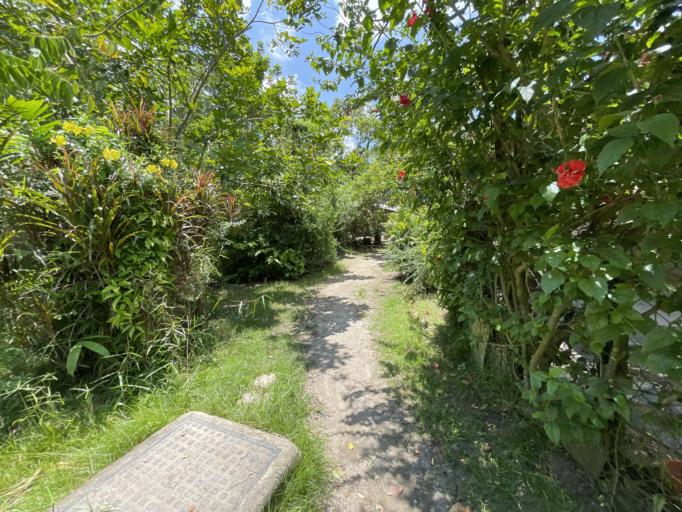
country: MY
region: Johor
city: Kampung Pasir Gudang Baru
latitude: 1.3843
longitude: 103.8793
